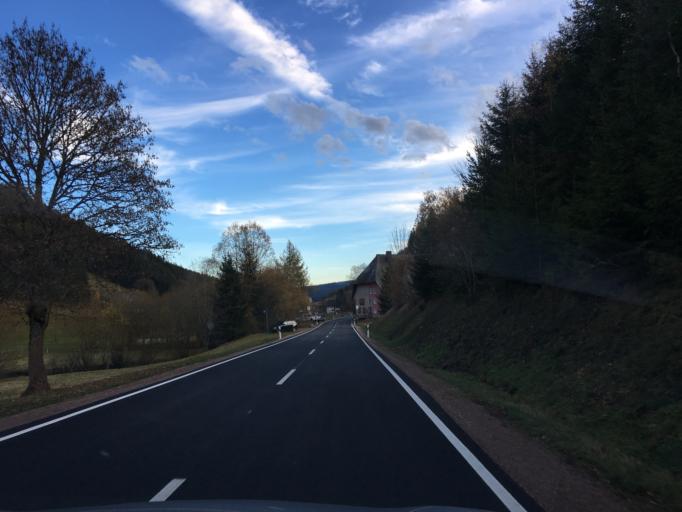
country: DE
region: Baden-Wuerttemberg
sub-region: Freiburg Region
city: Furtwangen im Schwarzwald
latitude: 48.0754
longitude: 8.1858
